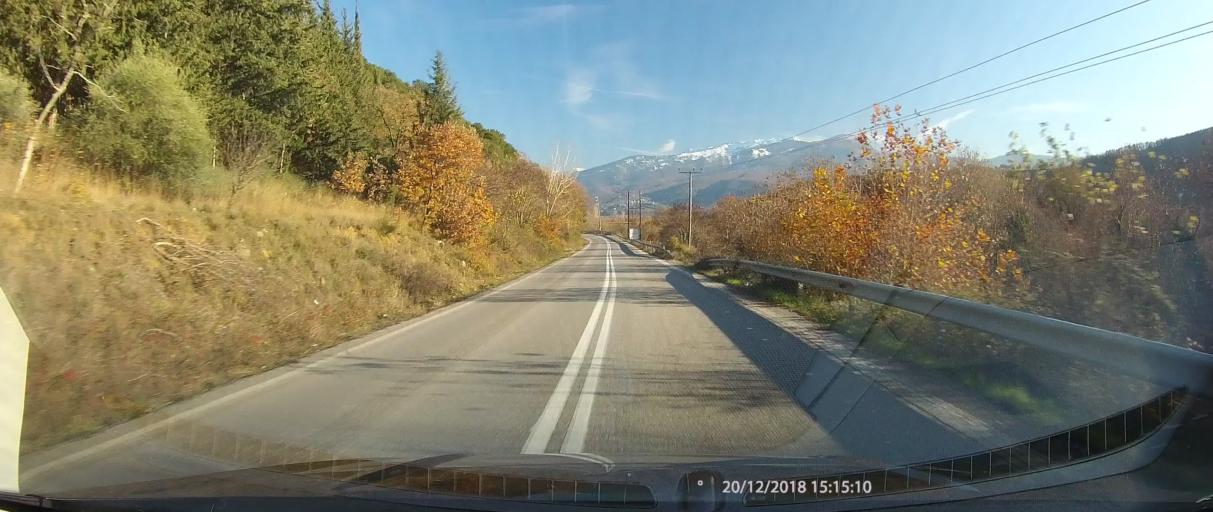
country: GR
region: Central Greece
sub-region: Nomos Fthiotidos
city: Makrakomi
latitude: 38.9301
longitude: 21.9882
